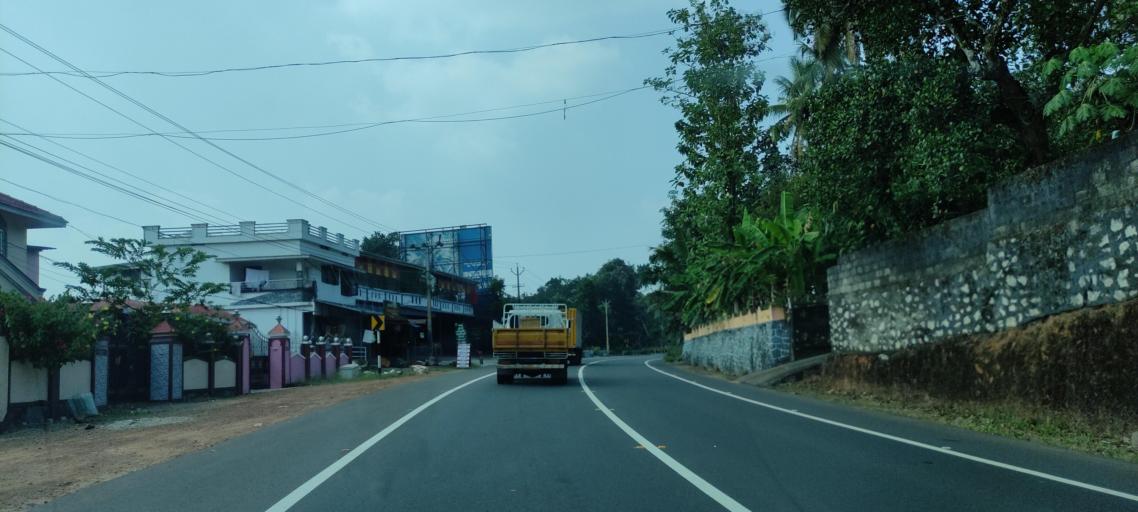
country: IN
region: Kerala
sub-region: Alappuzha
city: Chengannur
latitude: 9.2590
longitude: 76.6584
